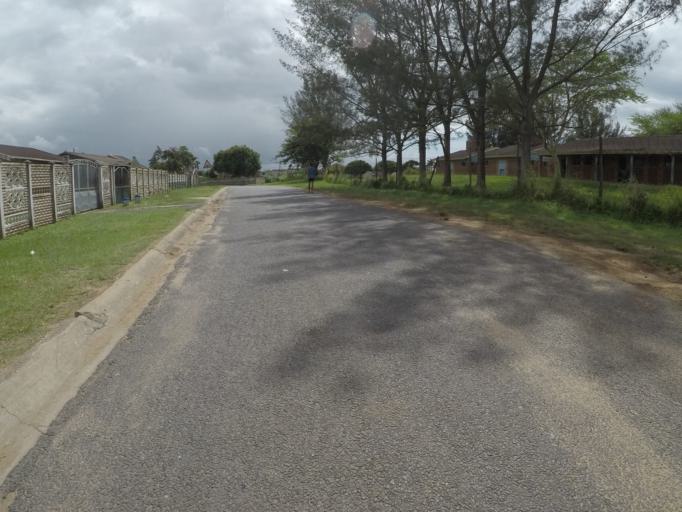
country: ZA
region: KwaZulu-Natal
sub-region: uThungulu District Municipality
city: eSikhawini
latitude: -28.8634
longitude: 31.9175
